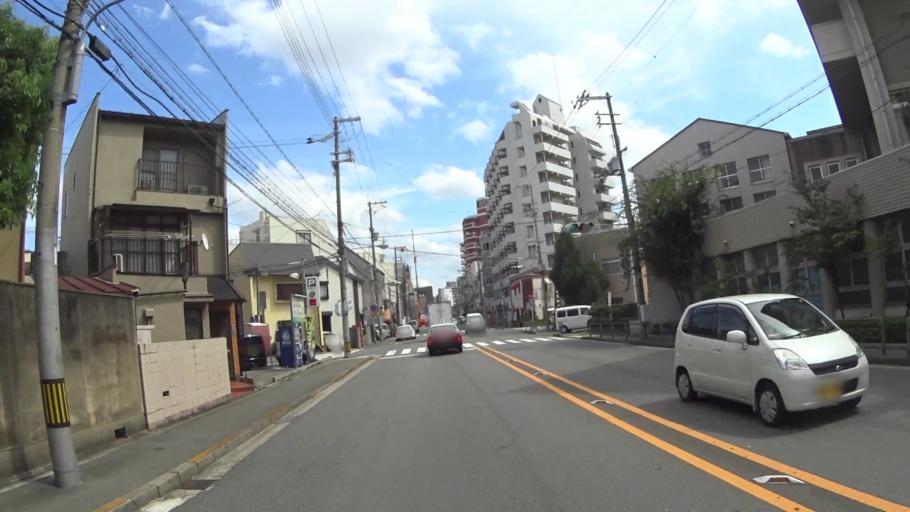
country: JP
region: Kyoto
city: Kyoto
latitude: 35.0077
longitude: 135.7438
